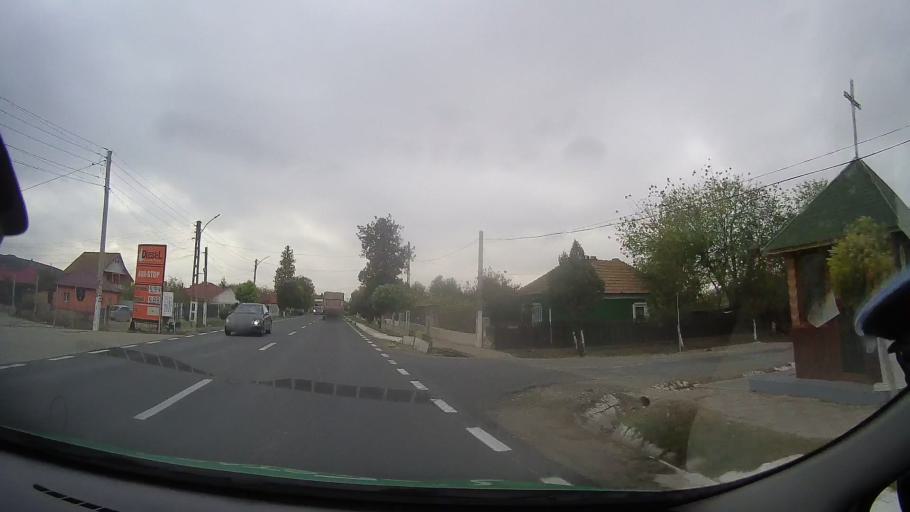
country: RO
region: Constanta
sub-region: Comuna Castelu
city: Castelu
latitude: 44.2576
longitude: 28.3415
